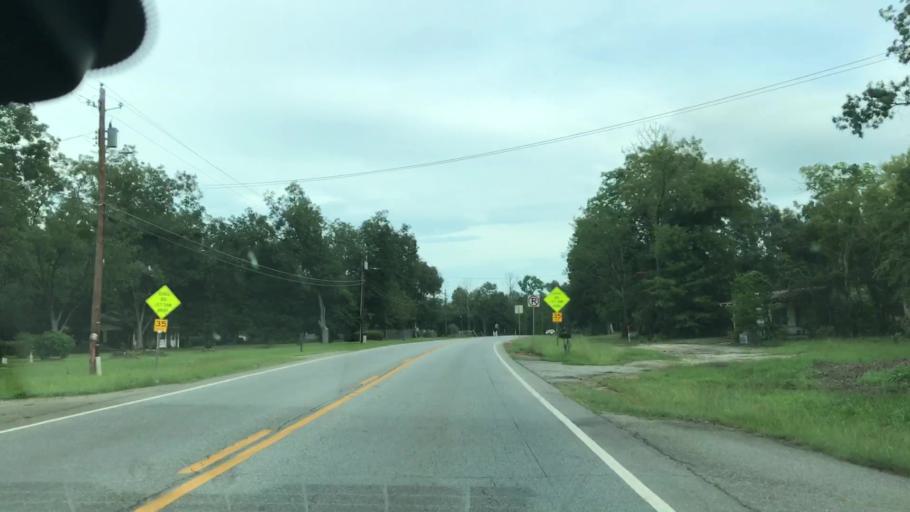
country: US
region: Georgia
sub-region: Quitman County
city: Georgetown
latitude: 31.8812
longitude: -85.0873
